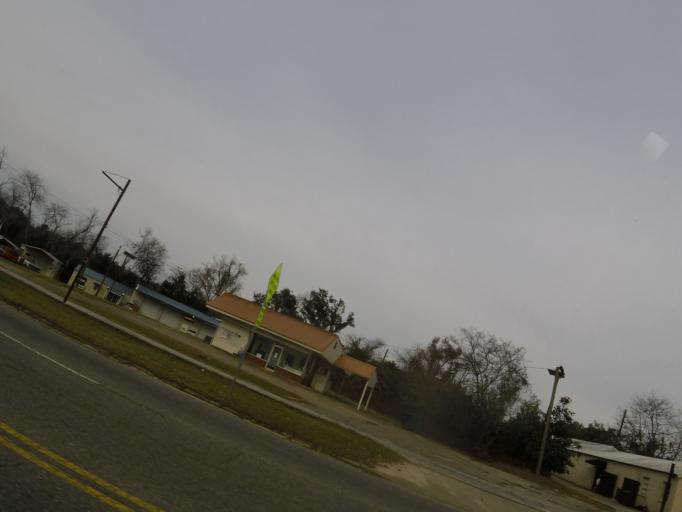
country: US
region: Georgia
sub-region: Decatur County
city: Bainbridge
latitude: 30.9095
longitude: -84.5770
